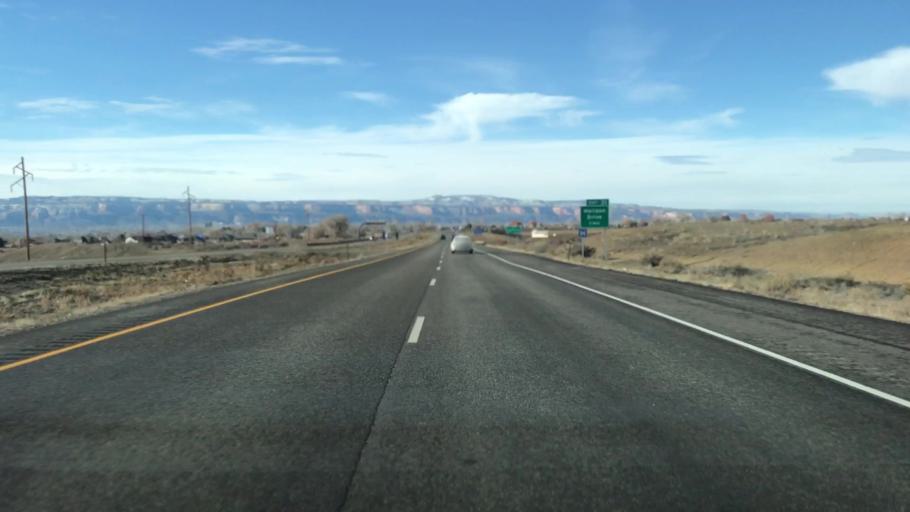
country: US
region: Colorado
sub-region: Mesa County
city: Fruitvale
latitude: 39.1064
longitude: -108.5223
